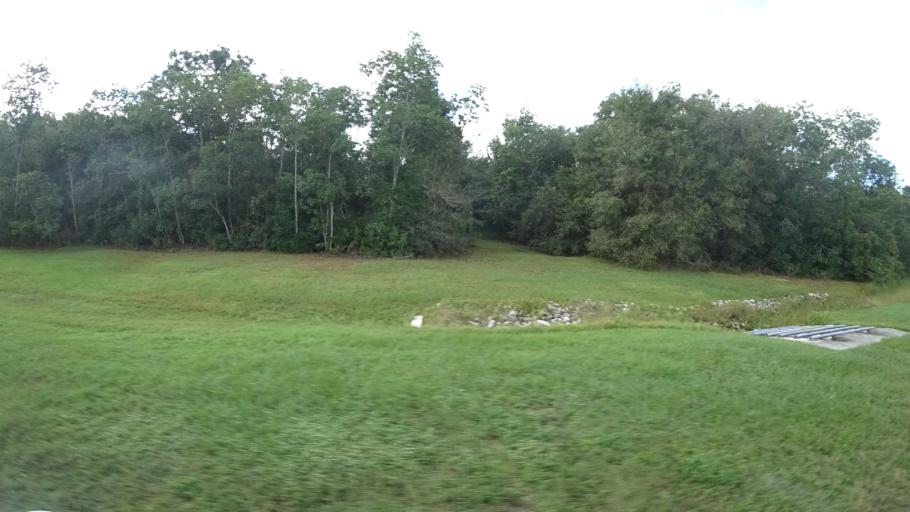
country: US
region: Florida
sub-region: Sarasota County
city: Lake Sarasota
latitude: 27.3630
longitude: -82.2459
